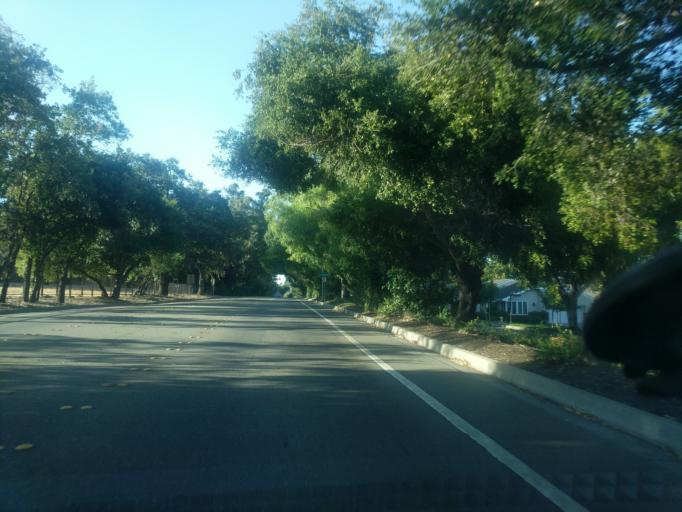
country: US
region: California
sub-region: Alameda County
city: Pleasanton
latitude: 37.6476
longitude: -121.9042
